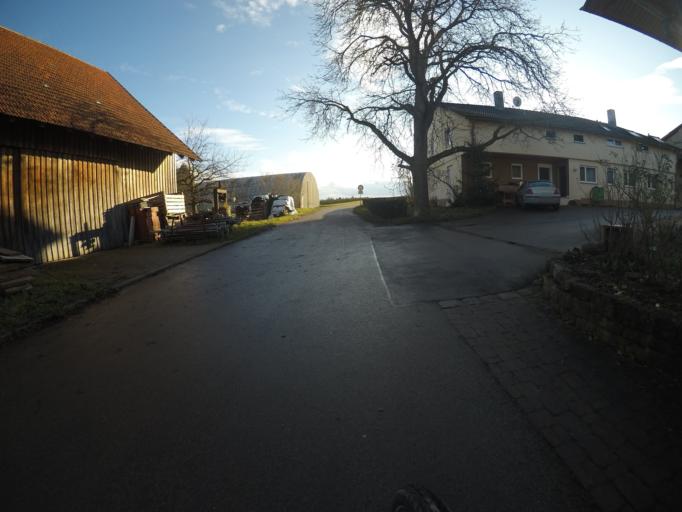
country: DE
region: Baden-Wuerttemberg
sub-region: Regierungsbezirk Stuttgart
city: Herrenberg
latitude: 48.5495
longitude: 8.8744
